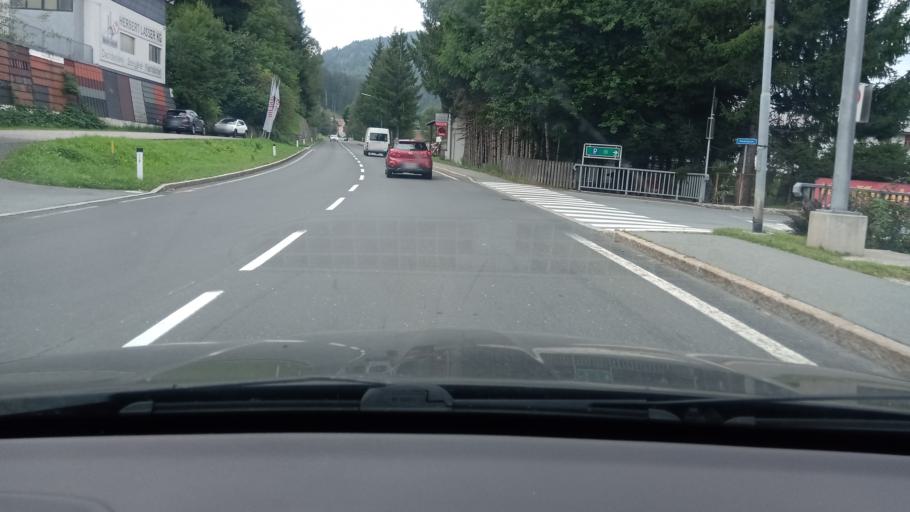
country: AT
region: Carinthia
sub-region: Politischer Bezirk Hermagor
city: Hermagor
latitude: 46.6260
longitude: 13.3699
